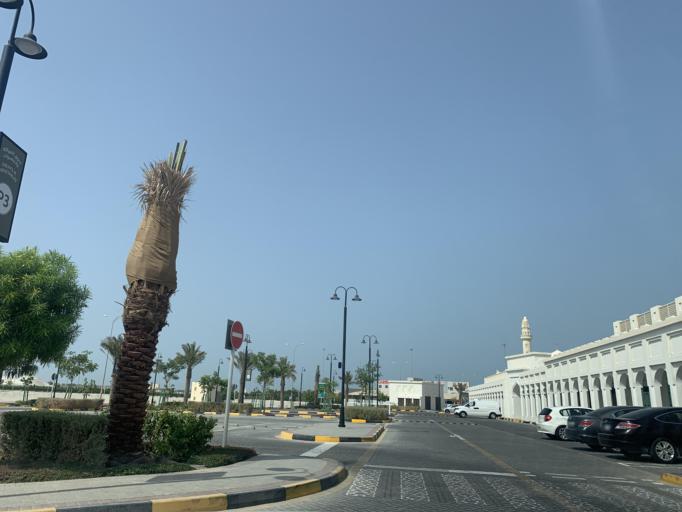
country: BH
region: Muharraq
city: Al Muharraq
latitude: 26.3053
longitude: 50.6372
